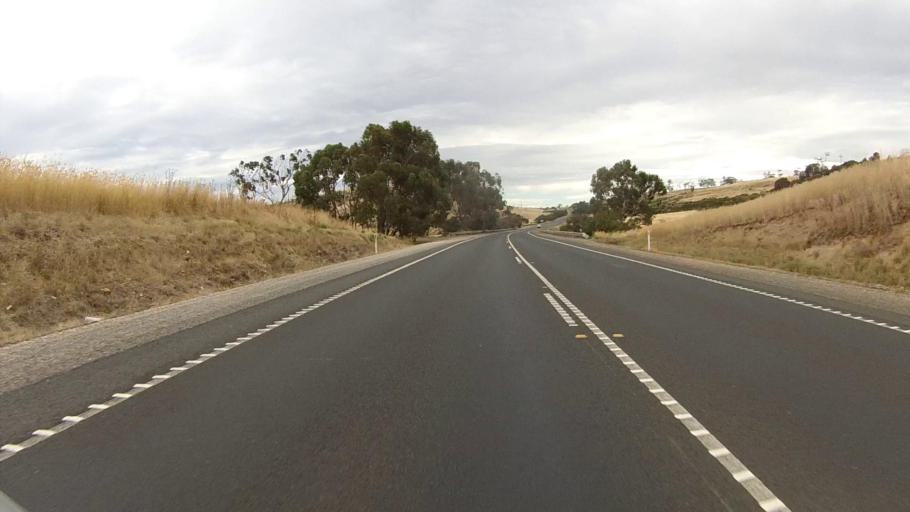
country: AU
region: Tasmania
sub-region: Brighton
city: Bridgewater
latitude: -42.3454
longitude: 147.3382
